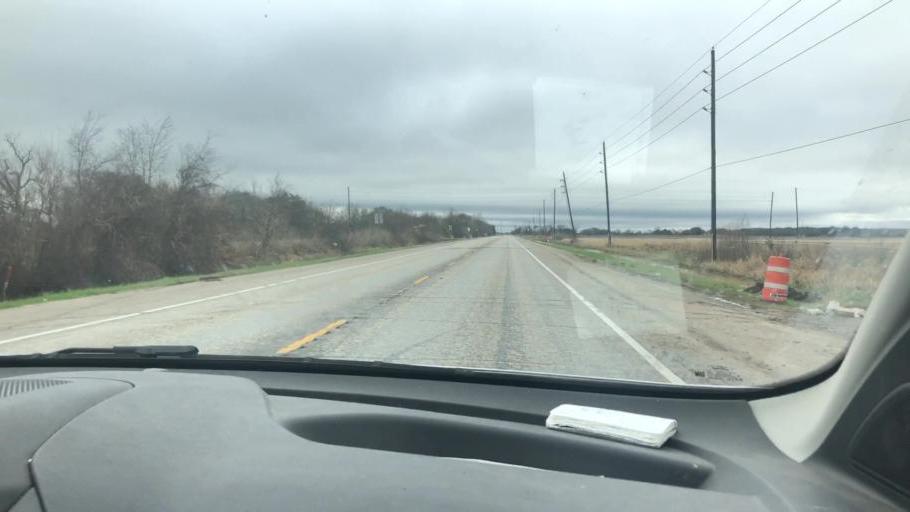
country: US
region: Texas
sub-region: Wharton County
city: Wharton
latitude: 29.2646
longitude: -96.0565
